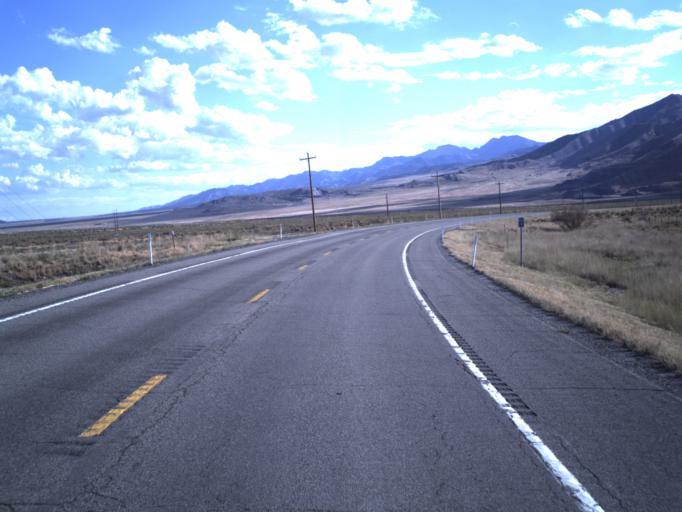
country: US
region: Utah
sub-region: Tooele County
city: Grantsville
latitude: 40.6981
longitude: -112.5299
